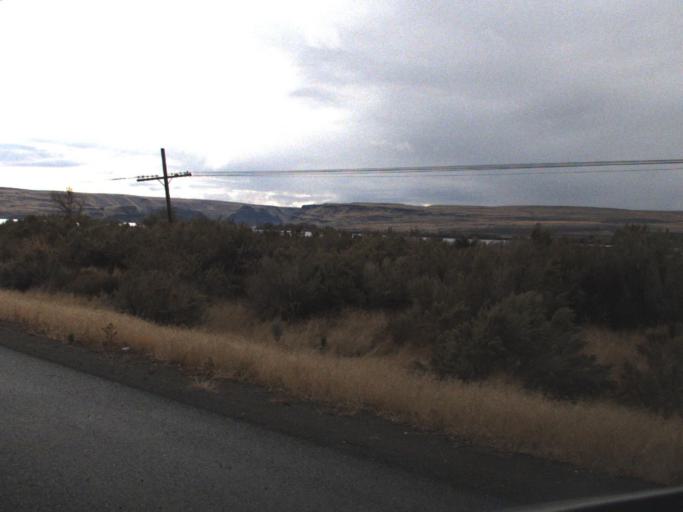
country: US
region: Washington
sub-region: Benton County
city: Finley
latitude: 46.1230
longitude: -118.9297
